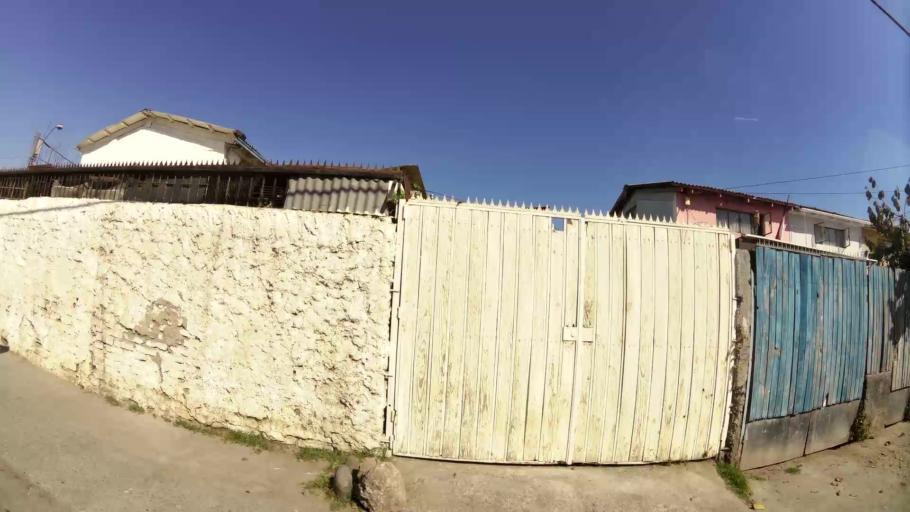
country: CL
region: Santiago Metropolitan
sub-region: Provincia de Santiago
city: La Pintana
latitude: -33.5606
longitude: -70.6195
